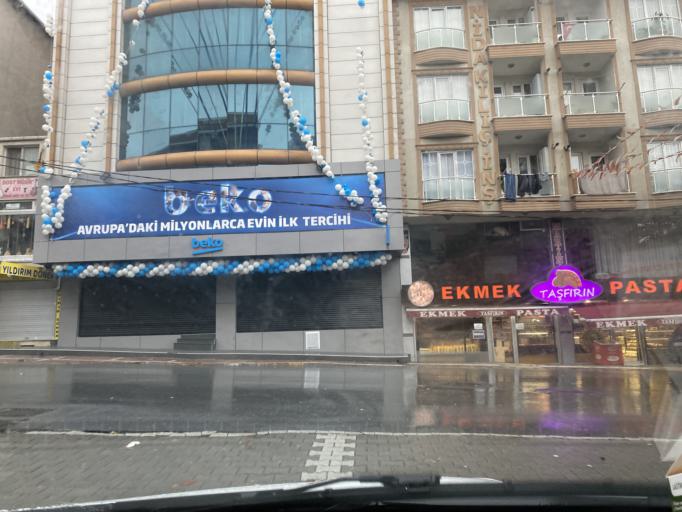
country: TR
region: Istanbul
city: Esenyurt
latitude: 41.0201
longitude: 28.6649
